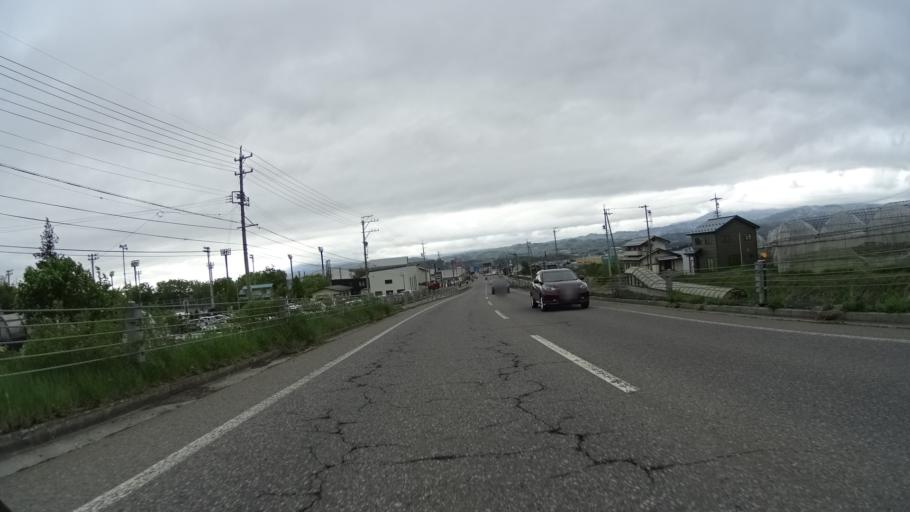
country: JP
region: Nagano
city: Nakano
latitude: 36.7585
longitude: 138.3839
